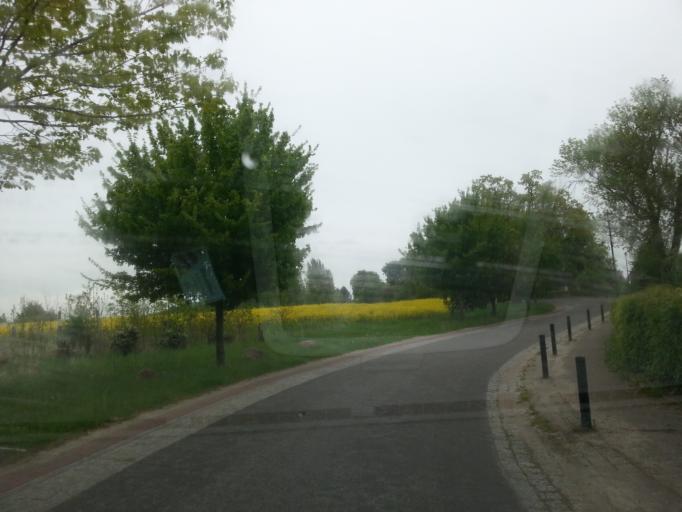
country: DE
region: Mecklenburg-Vorpommern
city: Malchow
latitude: 53.5153
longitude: 12.3858
